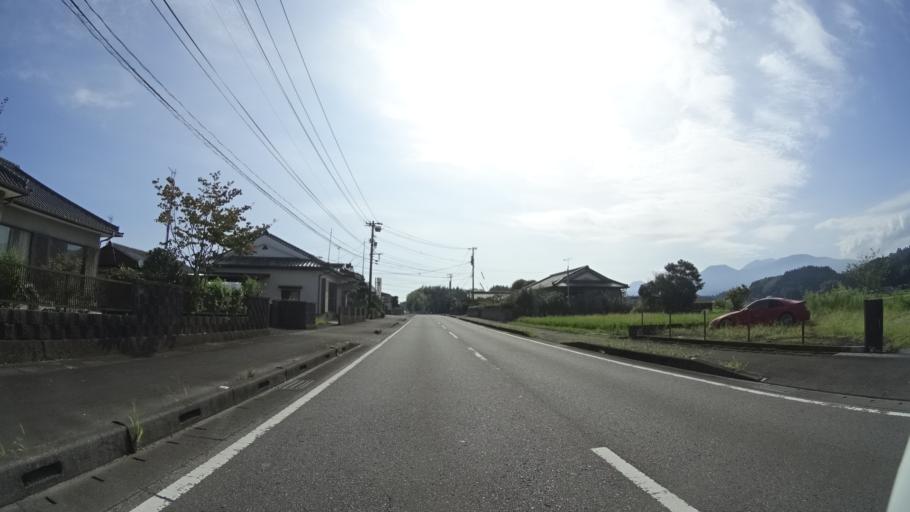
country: JP
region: Kagoshima
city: Okuchi-shinohara
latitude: 32.0417
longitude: 130.7862
